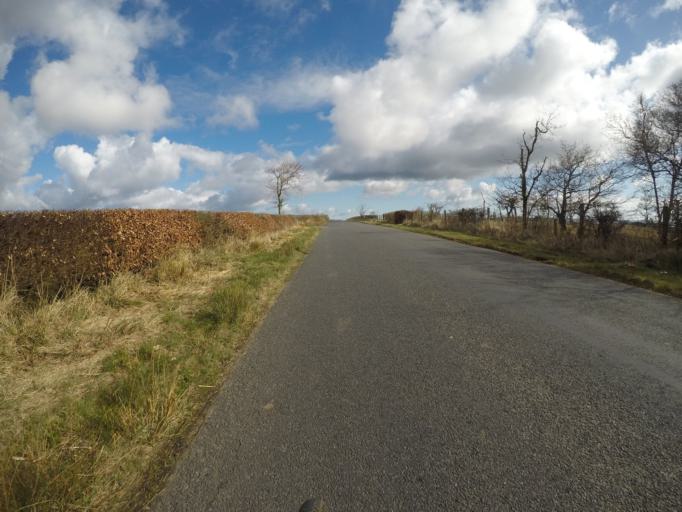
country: GB
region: Scotland
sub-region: North Ayrshire
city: Kilwinning
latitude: 55.6796
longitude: -4.6537
